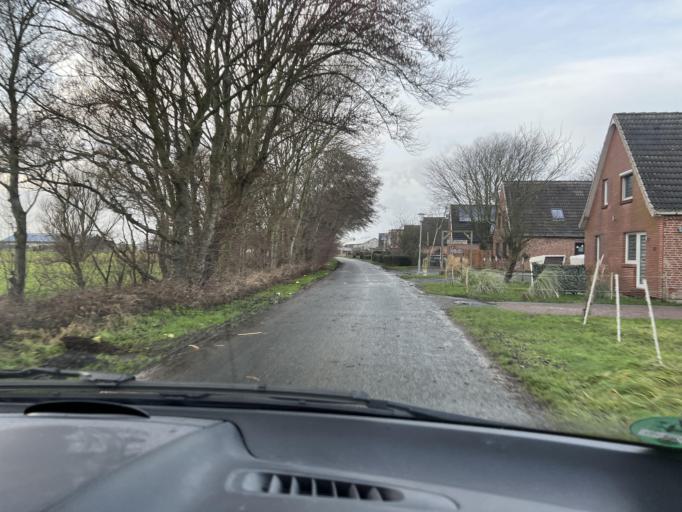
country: DE
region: Schleswig-Holstein
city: Hedwigenkoog
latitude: 54.1771
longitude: 8.8195
